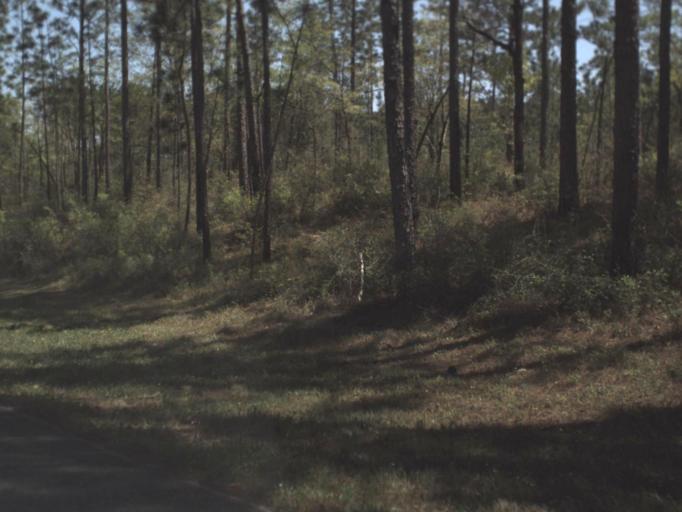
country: US
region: Florida
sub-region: Okaloosa County
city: Crestview
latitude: 30.8506
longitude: -86.7902
